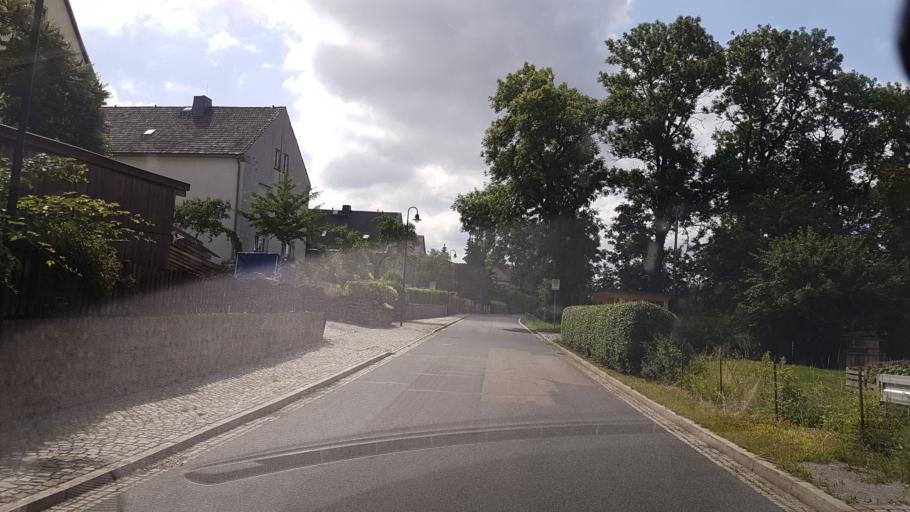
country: DE
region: Saxony
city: Wachau
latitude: 51.1647
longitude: 13.9069
